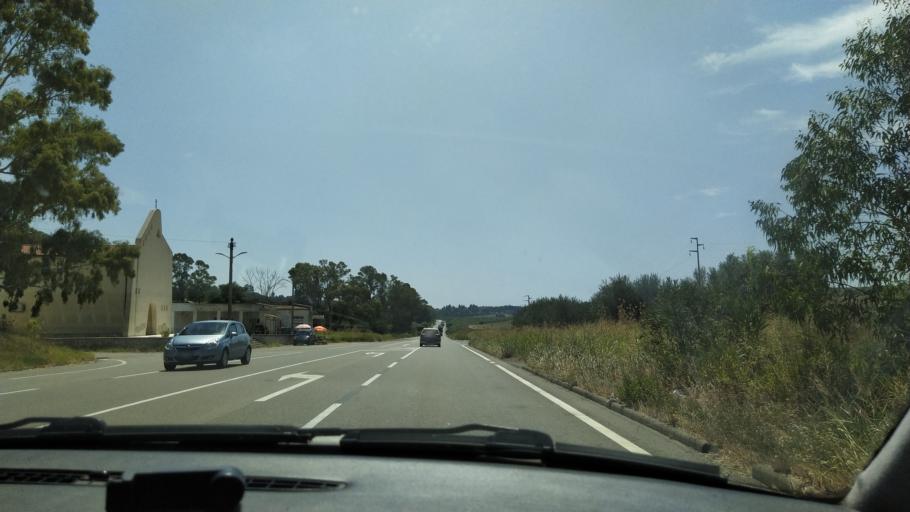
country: IT
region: Basilicate
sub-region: Provincia di Matera
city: Bernalda
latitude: 40.4444
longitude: 16.7799
